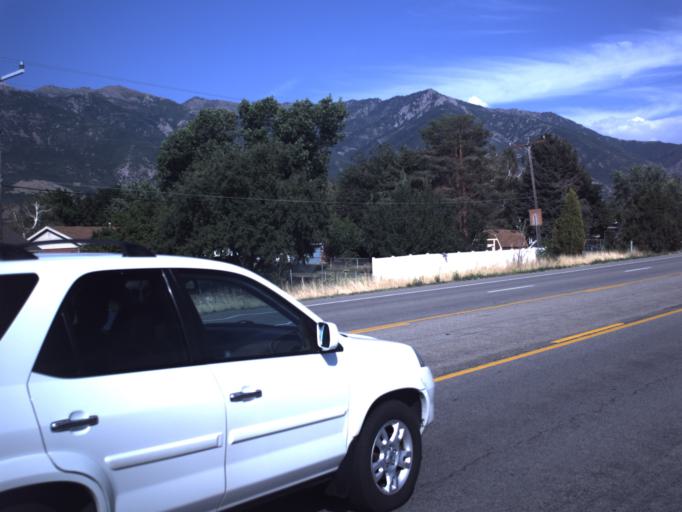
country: US
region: Utah
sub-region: Weber County
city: Washington Terrace
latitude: 41.1673
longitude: -111.9619
